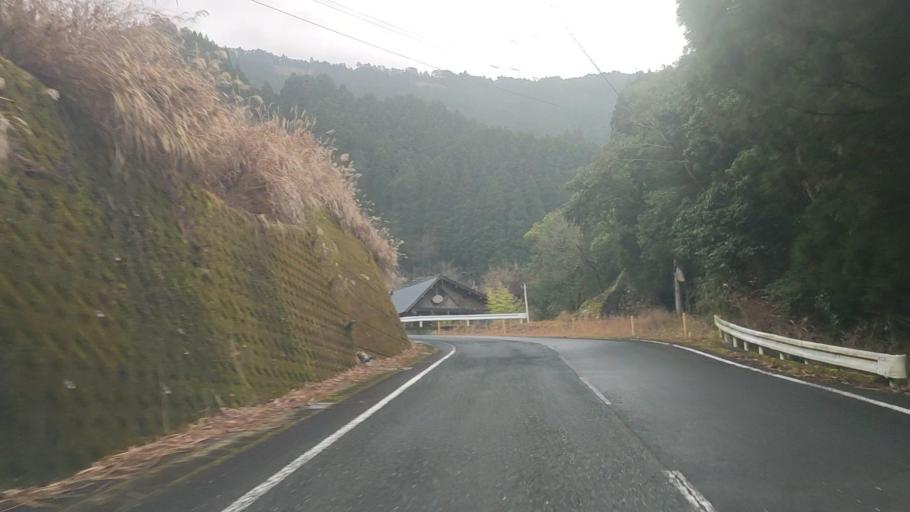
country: JP
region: Kumamoto
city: Matsubase
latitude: 32.6005
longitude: 130.8896
